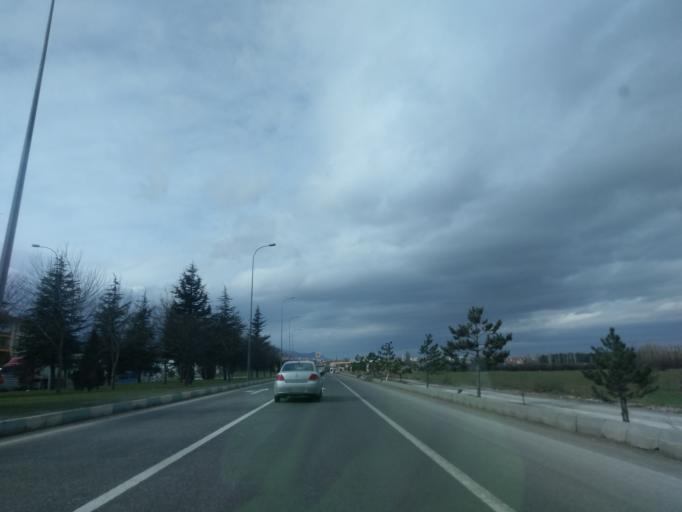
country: TR
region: Kuetahya
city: Kutahya
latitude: 39.4118
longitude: 30.0155
